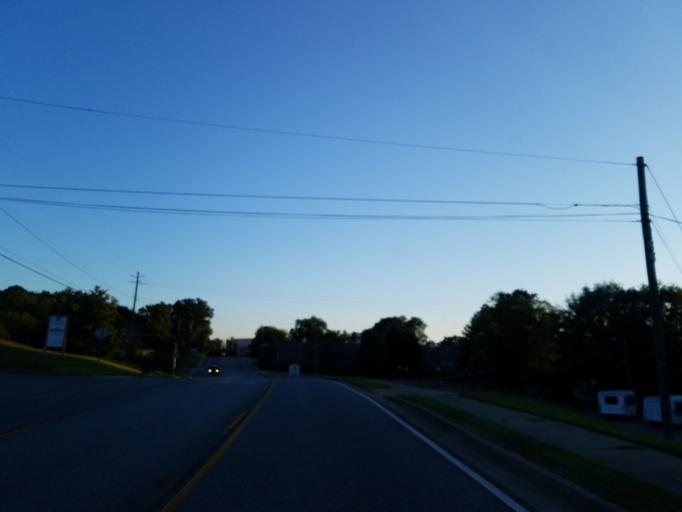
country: US
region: Georgia
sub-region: Forsyth County
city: Cumming
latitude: 34.2106
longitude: -84.1337
